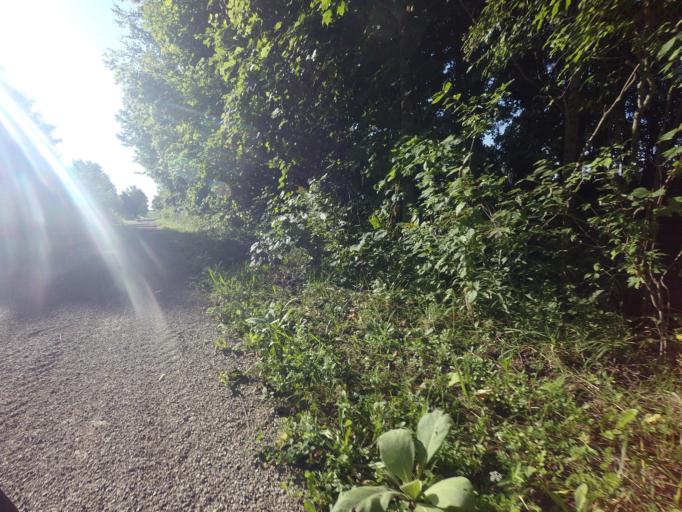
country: CA
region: Ontario
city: Goderich
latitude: 43.7474
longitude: -81.4972
